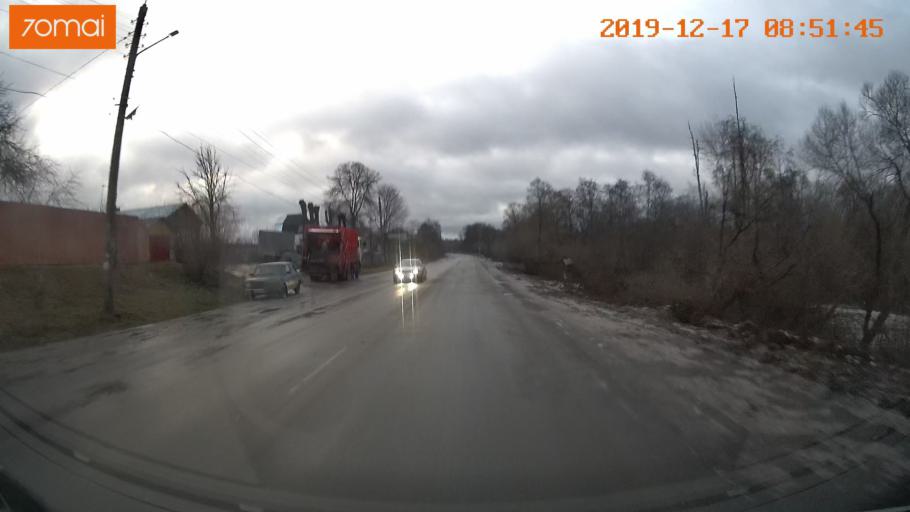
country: RU
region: Vladimir
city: Kosterevo
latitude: 55.9551
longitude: 39.6328
